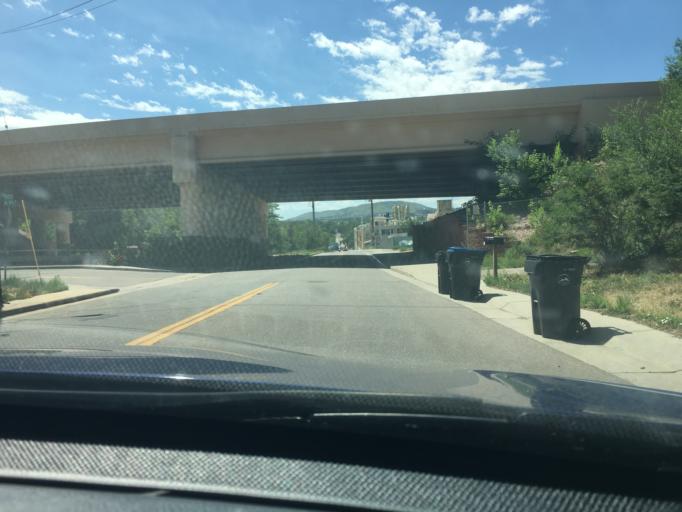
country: US
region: Colorado
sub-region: Jefferson County
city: Golden
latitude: 39.7617
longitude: -105.2240
